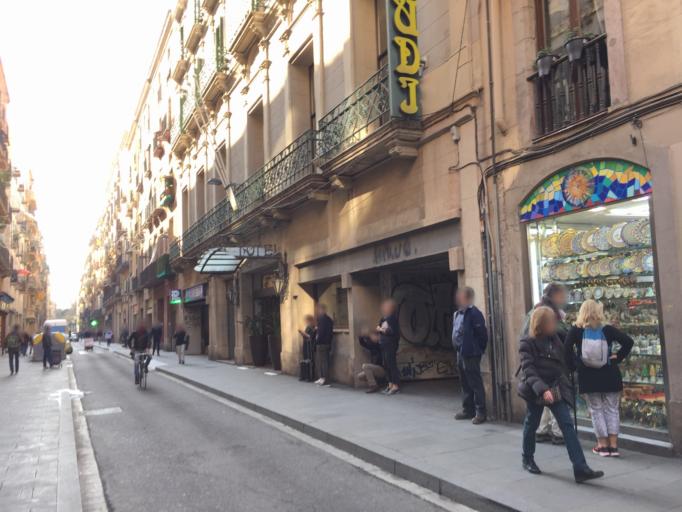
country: ES
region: Catalonia
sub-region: Provincia de Barcelona
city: Ciutat Vella
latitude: 41.3791
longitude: 2.1741
